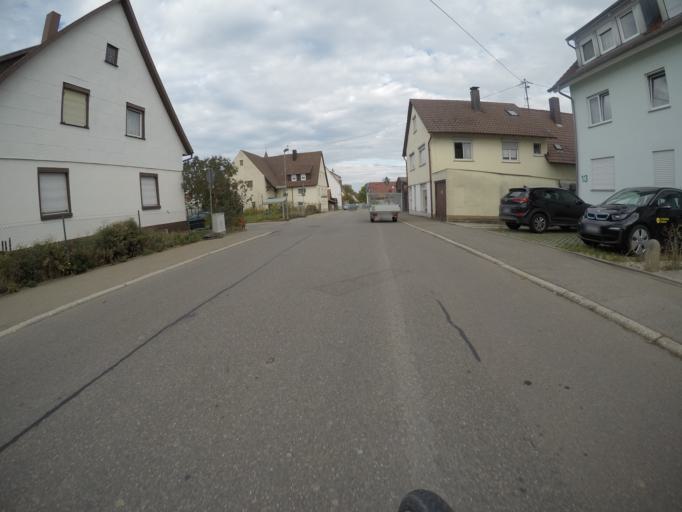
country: DE
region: Baden-Wuerttemberg
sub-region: Regierungsbezirk Stuttgart
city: Nufringen
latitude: 48.6214
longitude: 8.8894
